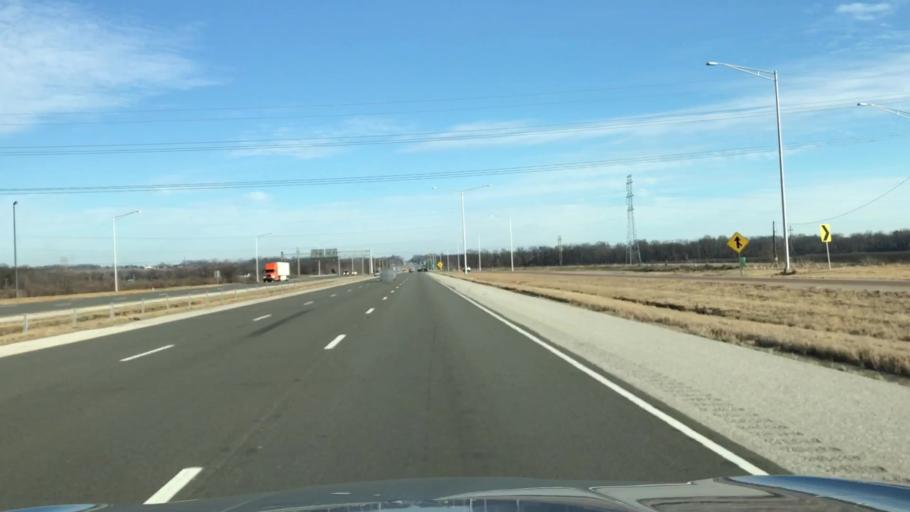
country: US
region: Illinois
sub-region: Madison County
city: Mitchell
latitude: 38.7569
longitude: -90.0395
